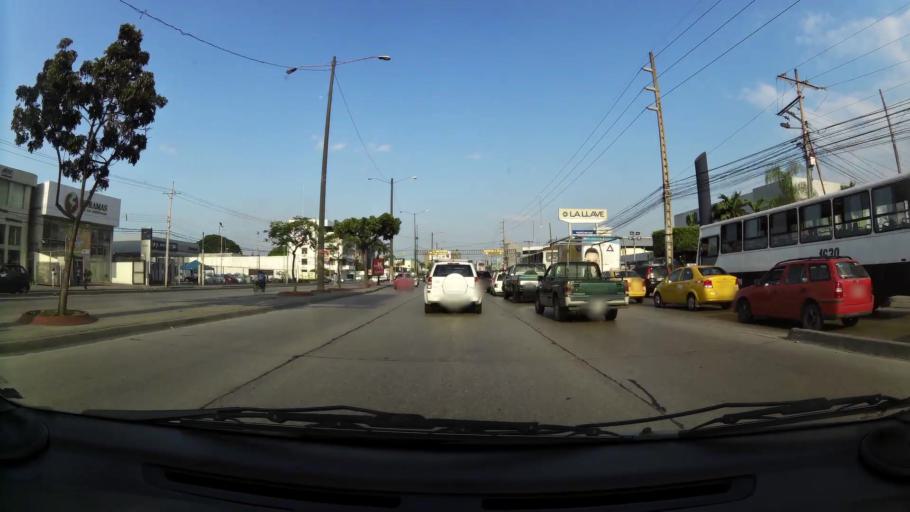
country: EC
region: Guayas
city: Eloy Alfaro
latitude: -2.1492
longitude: -79.9019
